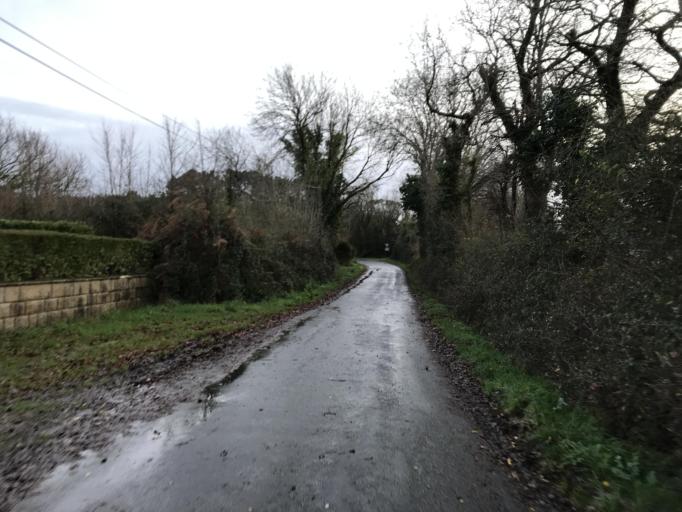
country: FR
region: Brittany
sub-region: Departement du Finistere
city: Logonna-Daoulas
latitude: 48.3229
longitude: -4.3119
